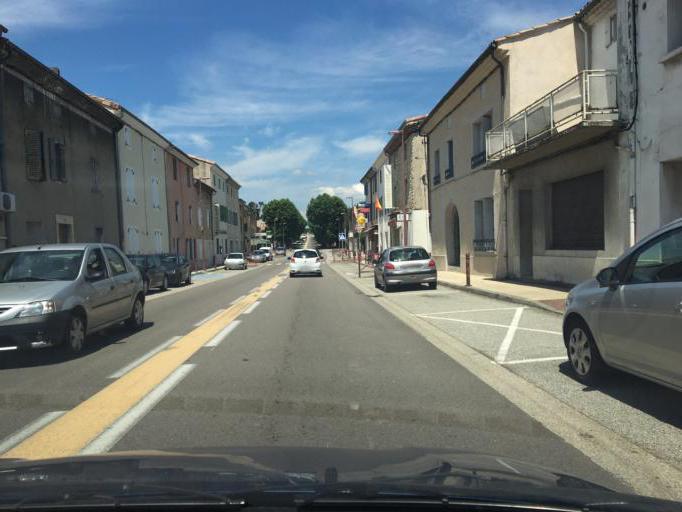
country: FR
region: Rhone-Alpes
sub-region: Departement de la Drome
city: Saulce-sur-Rhone
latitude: 44.7039
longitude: 4.7994
